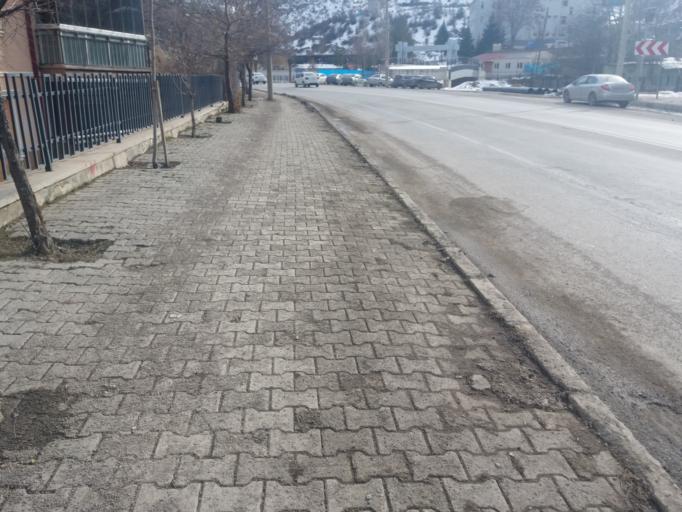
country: TR
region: Gumushane
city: Gumushkhane
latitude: 40.4477
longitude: 39.4979
